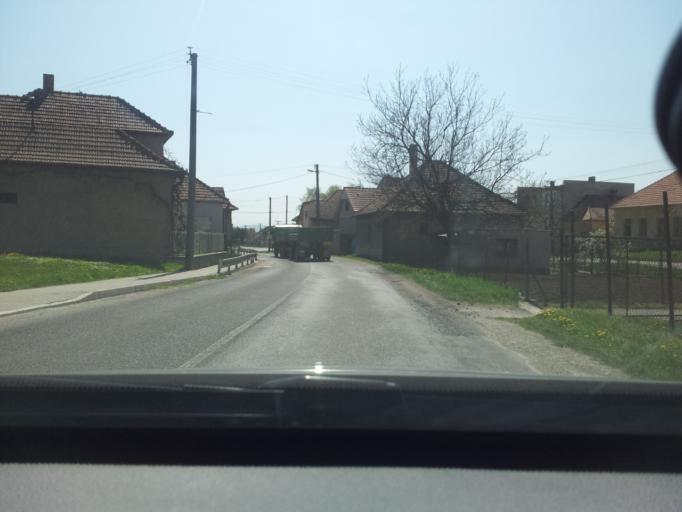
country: SK
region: Nitriansky
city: Banovce nad Bebravou
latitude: 48.6227
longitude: 18.2482
